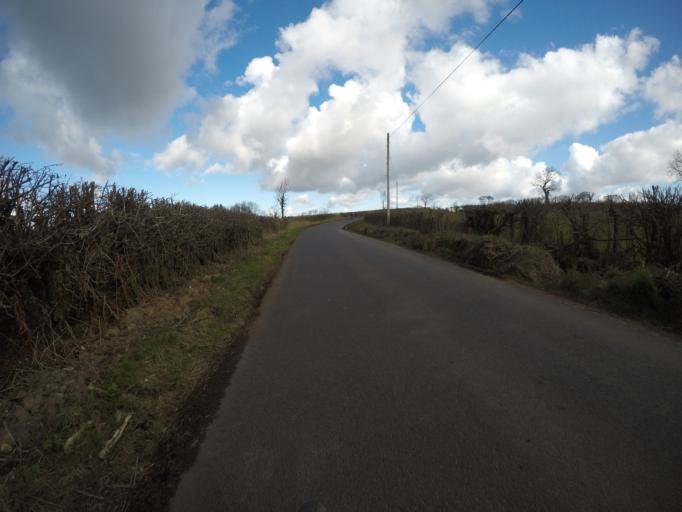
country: GB
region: Scotland
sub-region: North Ayrshire
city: Dalry
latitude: 55.6931
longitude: -4.6745
